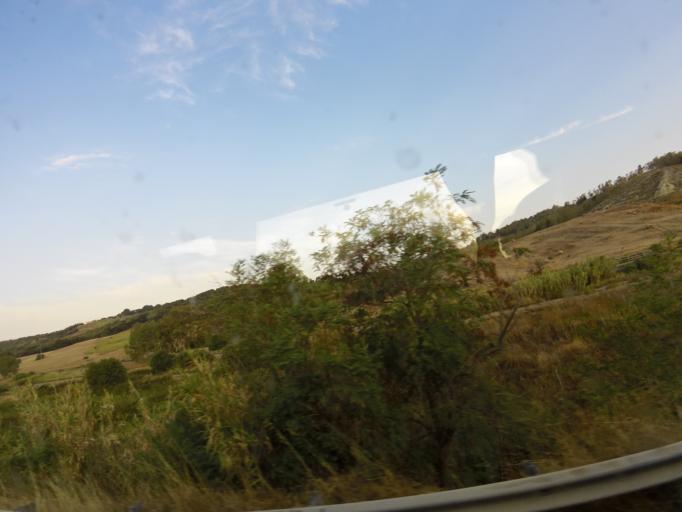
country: IT
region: Calabria
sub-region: Provincia di Reggio Calabria
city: Riace Marina
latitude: 38.3732
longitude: 16.5094
